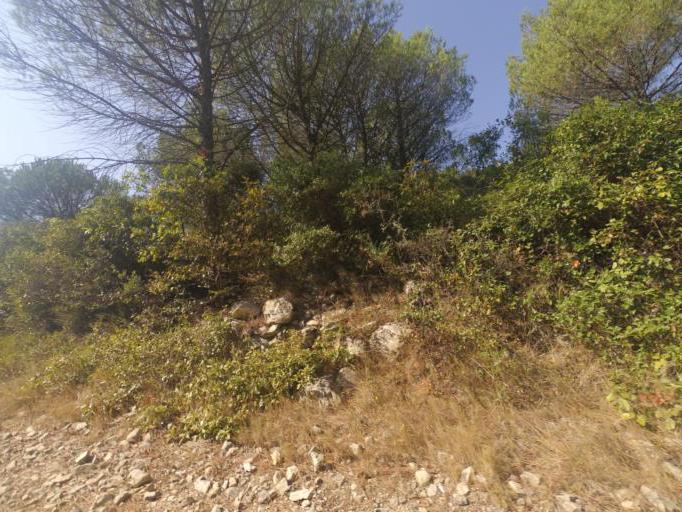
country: FR
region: Languedoc-Roussillon
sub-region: Departement du Gard
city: Congenies
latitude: 43.7622
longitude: 4.1912
